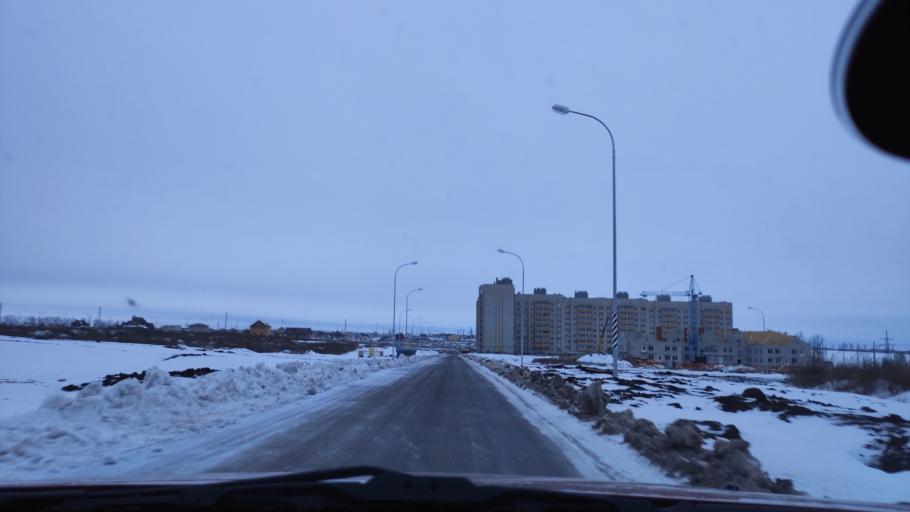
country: RU
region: Tambov
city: Tambov
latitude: 52.7809
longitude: 41.4209
